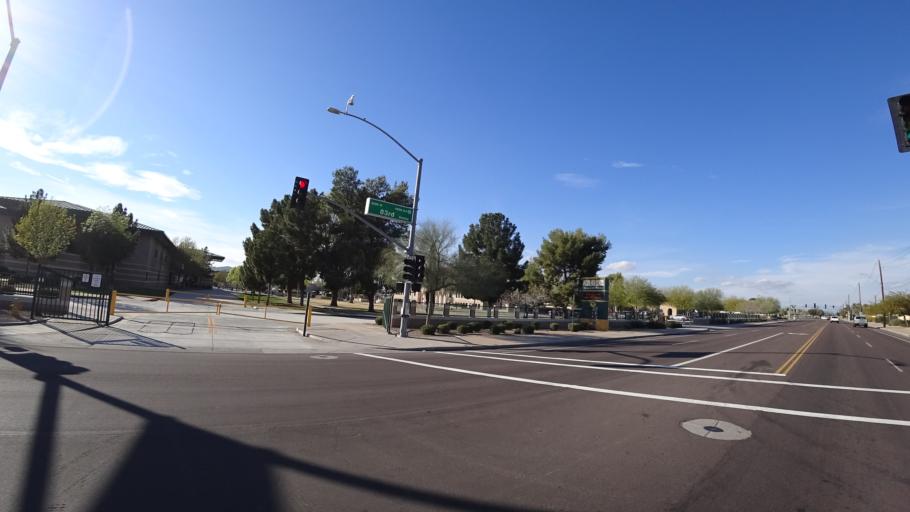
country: US
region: Arizona
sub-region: Maricopa County
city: Peoria
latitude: 33.5862
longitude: -112.2377
